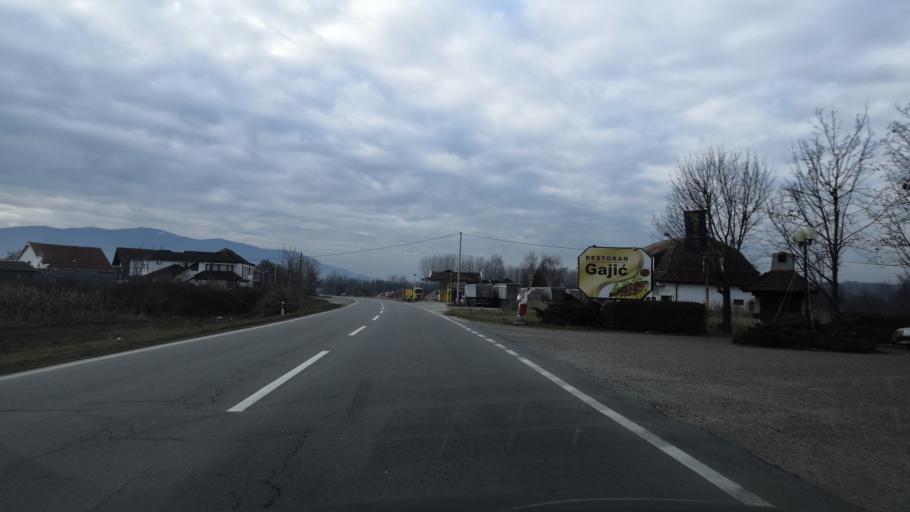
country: RS
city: Lipnicki Sor
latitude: 44.5650
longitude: 19.2020
